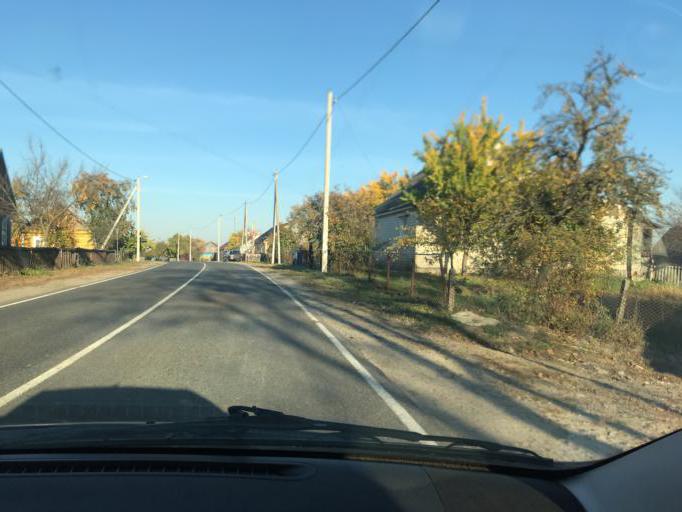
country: BY
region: Brest
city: Stolin
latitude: 51.8336
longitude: 26.7279
